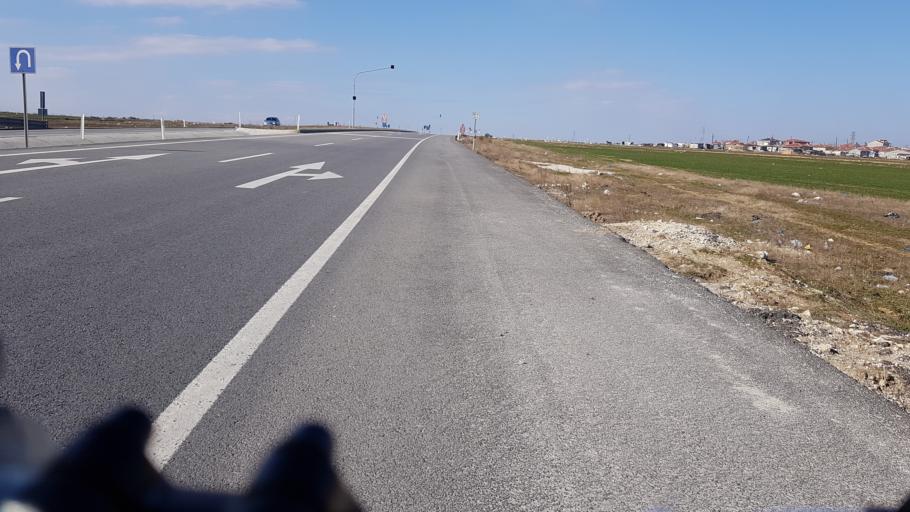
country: TR
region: Tekirdag
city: Saray
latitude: 41.4287
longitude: 27.9109
